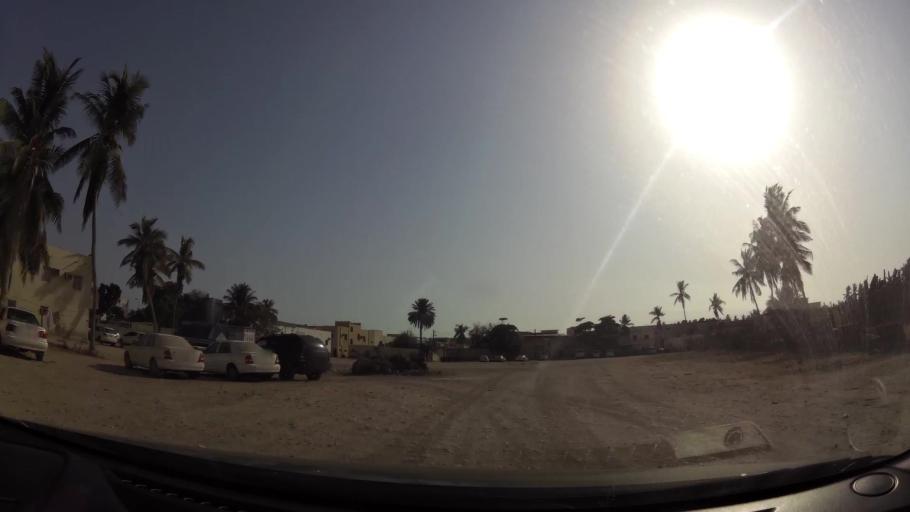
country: OM
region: Zufar
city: Salalah
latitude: 17.0033
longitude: 54.1043
